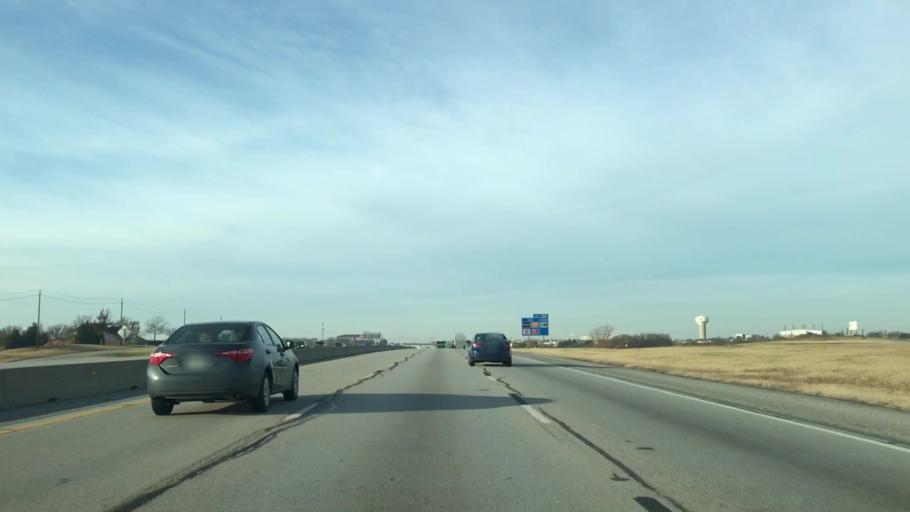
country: US
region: Texas
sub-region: Tarrant County
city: Sansom Park
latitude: 32.8212
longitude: -97.3973
